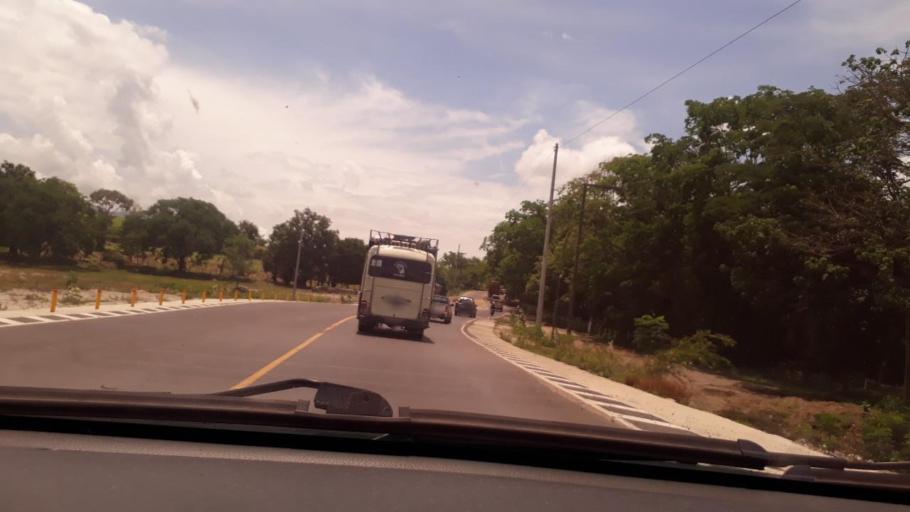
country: GT
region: Zacapa
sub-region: Municipio de Zacapa
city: Gualan
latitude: 15.0934
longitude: -89.4372
